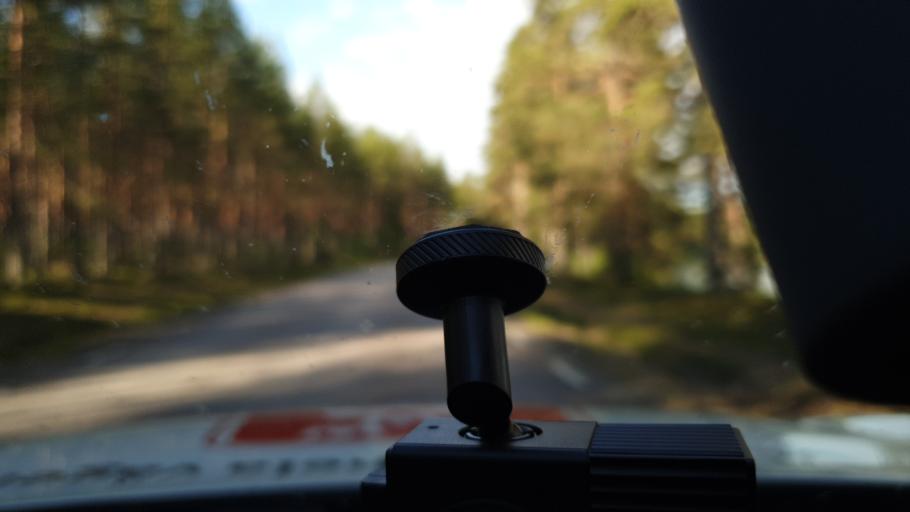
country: SE
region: Vaermland
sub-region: Torsby Kommun
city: Torsby
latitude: 59.9988
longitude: 12.8923
